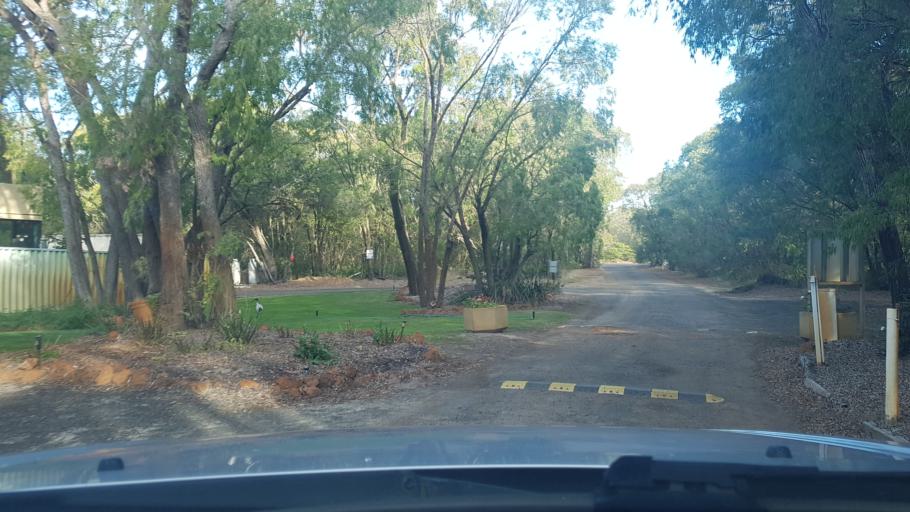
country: AU
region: Western Australia
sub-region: Busselton
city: Vasse
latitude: -33.6573
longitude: 115.2367
